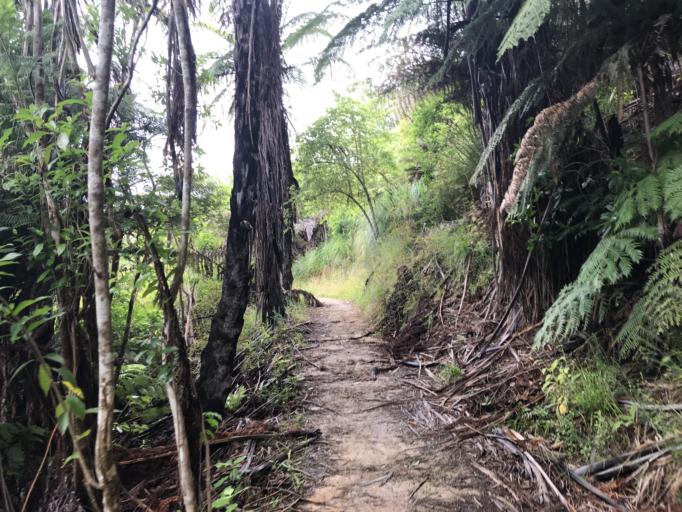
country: NZ
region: Marlborough
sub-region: Marlborough District
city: Picton
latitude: -41.2298
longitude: 173.9581
